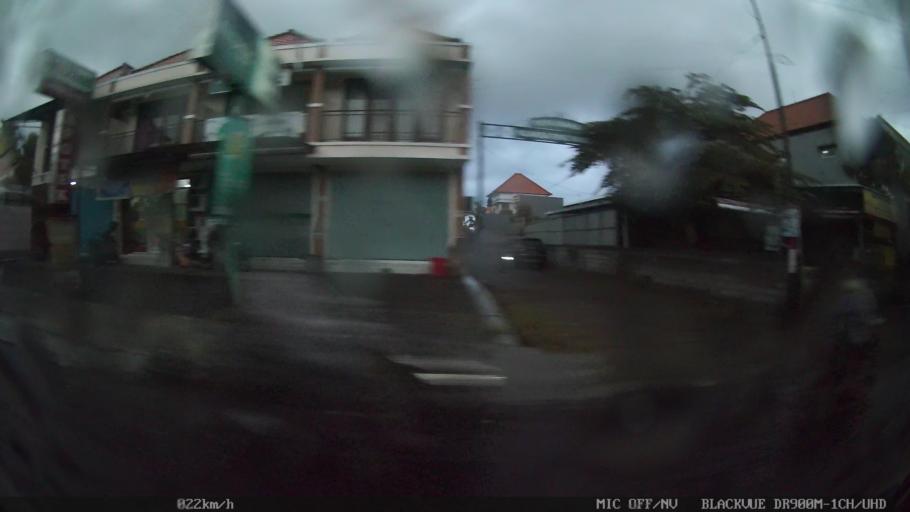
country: ID
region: Bali
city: Banjar Kayangan
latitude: -8.6136
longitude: 115.2220
